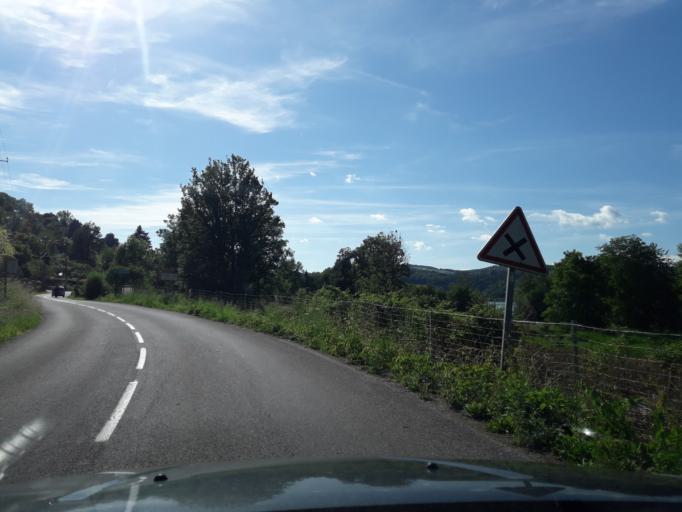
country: FR
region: Rhone-Alpes
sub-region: Departement de la Savoie
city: La Bridoire
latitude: 45.5382
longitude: 5.7944
